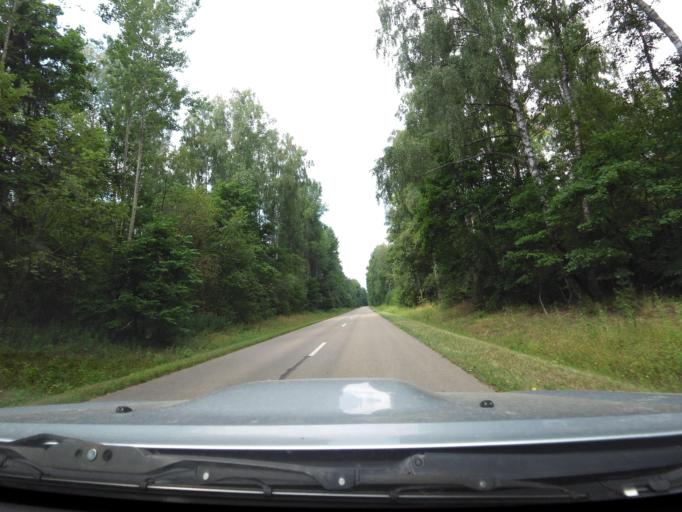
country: RU
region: Kaliningrad
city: Neman
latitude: 55.0892
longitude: 22.0354
